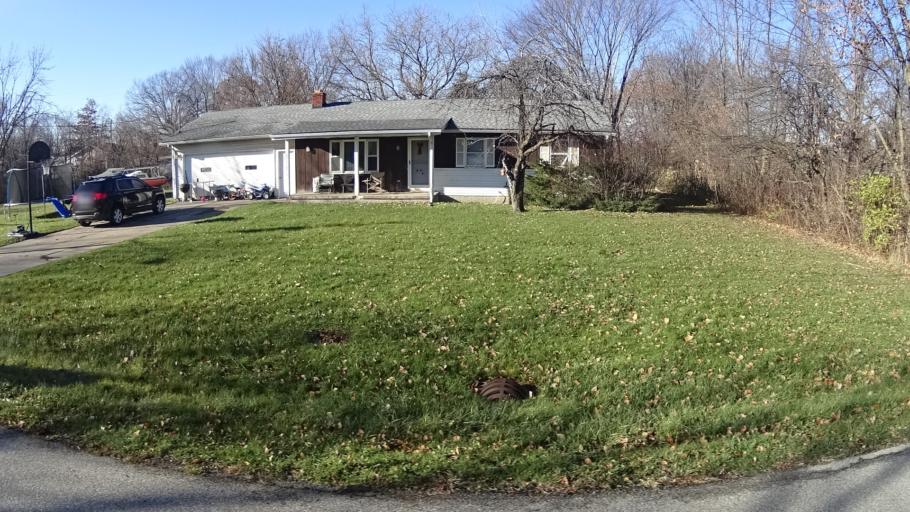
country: US
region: Ohio
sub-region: Lorain County
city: Sheffield
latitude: 41.4518
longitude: -82.1016
